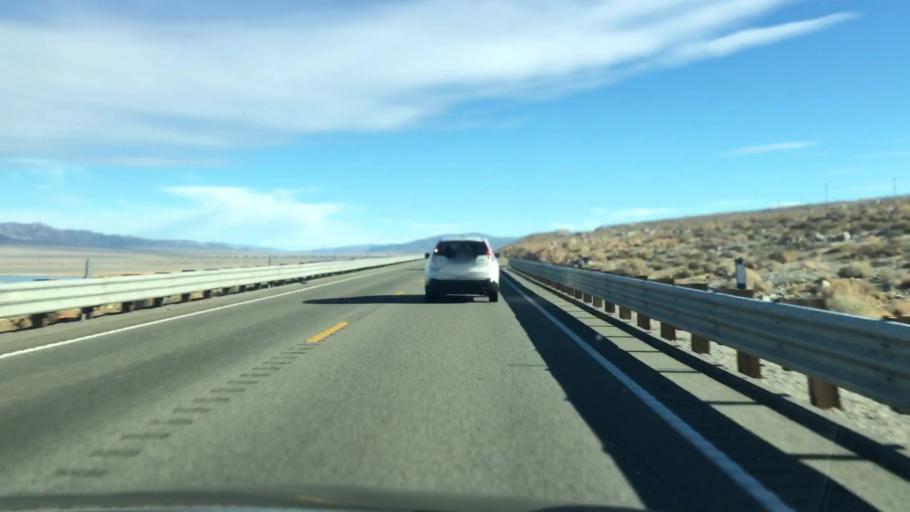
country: US
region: Nevada
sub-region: Mineral County
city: Hawthorne
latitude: 38.6156
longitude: -118.7283
